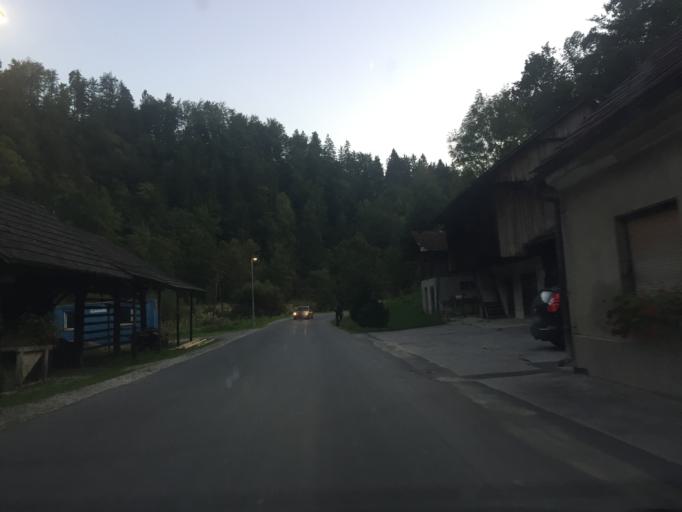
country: SI
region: Sostanj
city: Sostanj
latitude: 46.3714
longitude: 15.0231
